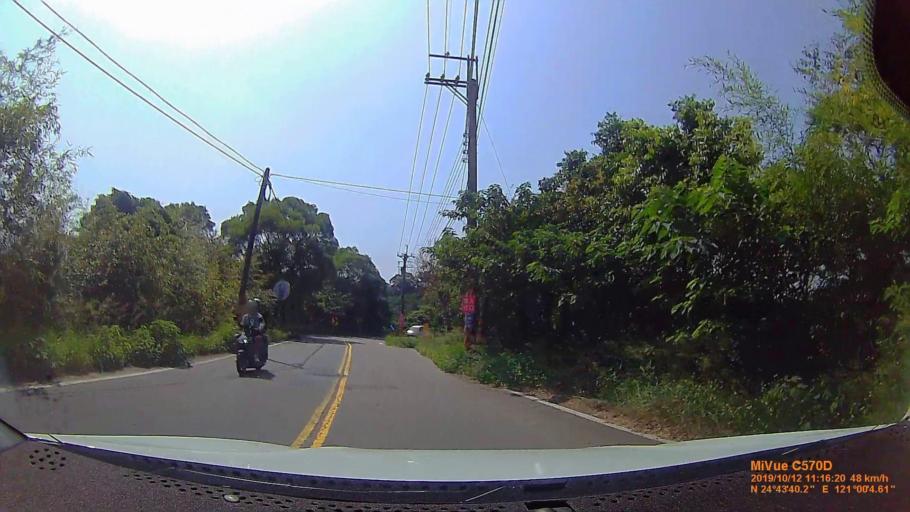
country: TW
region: Taiwan
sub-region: Hsinchu
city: Hsinchu
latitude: 24.7277
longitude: 121.0012
